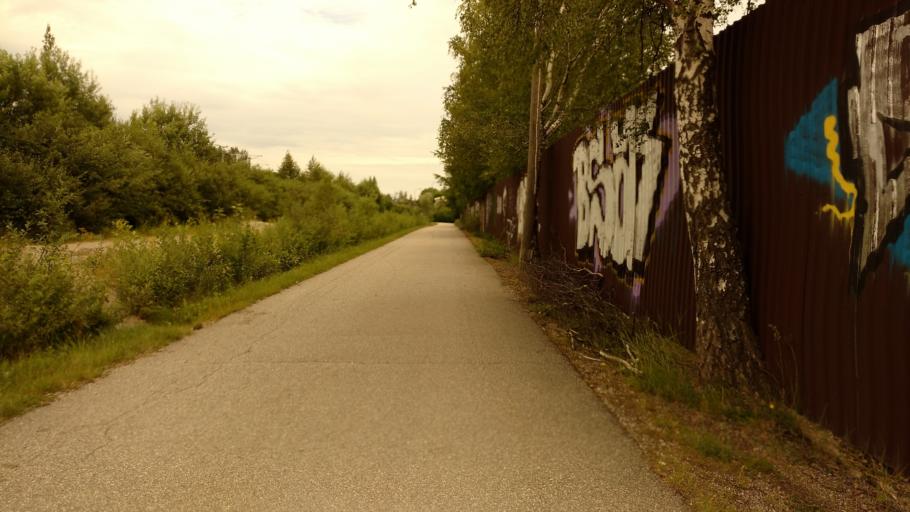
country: FI
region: Varsinais-Suomi
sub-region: Salo
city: Salo
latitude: 60.3767
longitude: 23.1229
